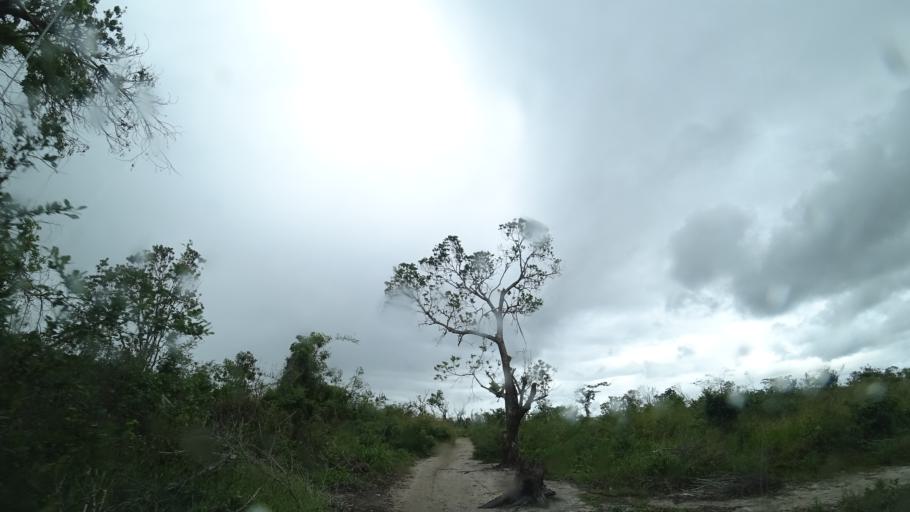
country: MZ
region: Sofala
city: Dondo
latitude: -19.5522
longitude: 35.0646
